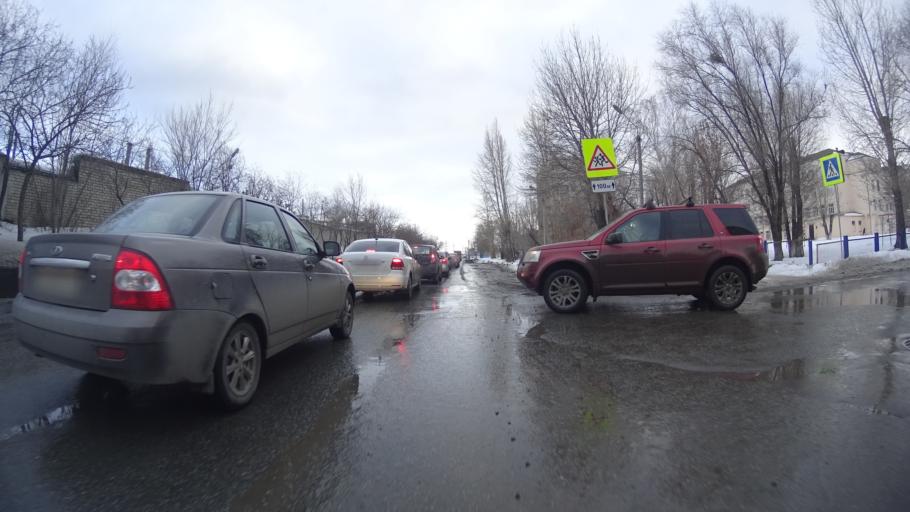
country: RU
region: Chelyabinsk
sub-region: Gorod Chelyabinsk
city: Chelyabinsk
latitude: 55.1421
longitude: 61.4011
